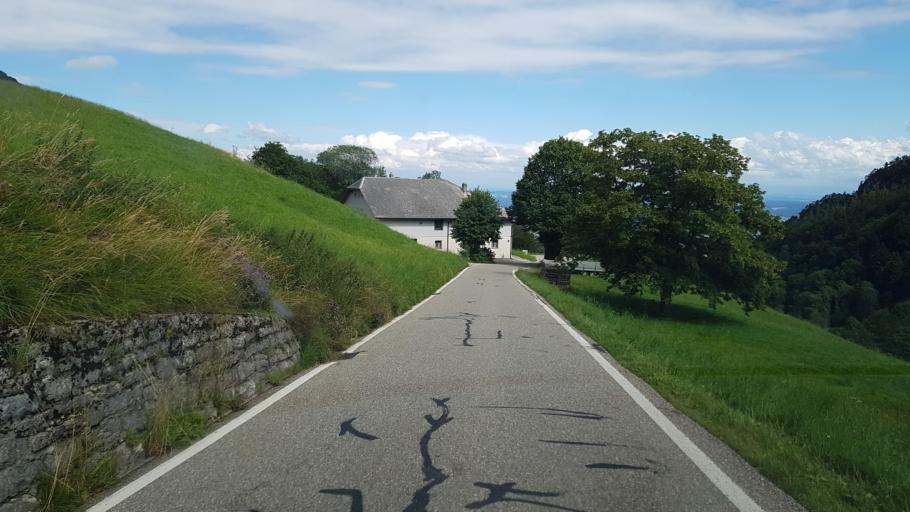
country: CH
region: Solothurn
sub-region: Bezirk Thal
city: Welschenrohr
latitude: 47.2624
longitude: 7.5430
